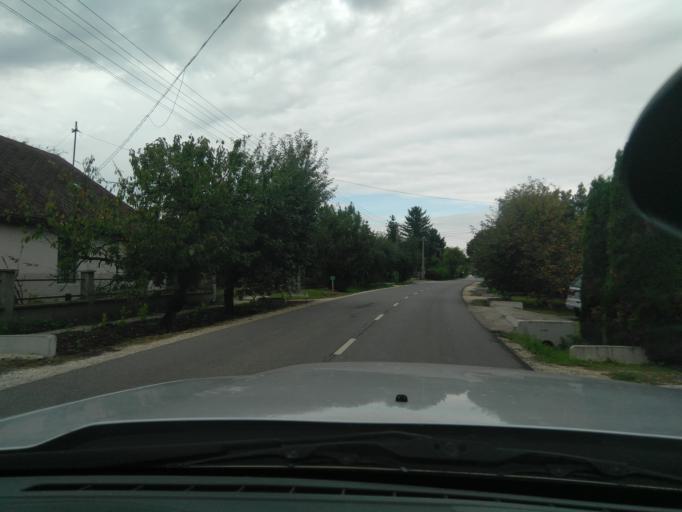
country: HU
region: Fejer
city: Martonvasar
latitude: 47.3439
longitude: 18.7425
